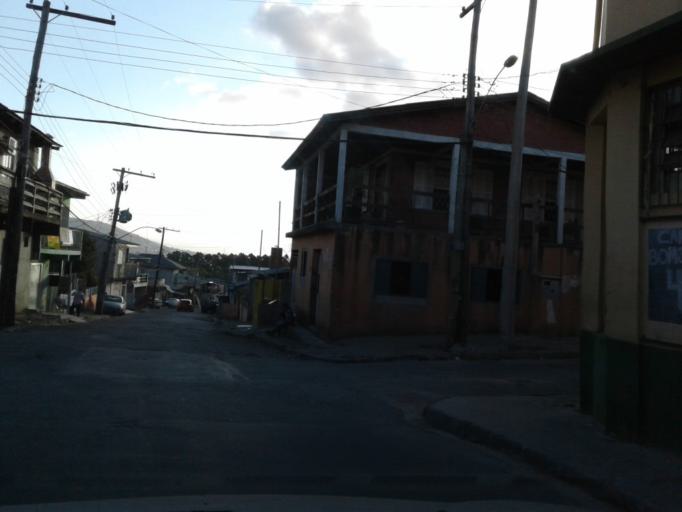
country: BR
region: Rio Grande do Sul
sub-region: Porto Alegre
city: Porto Alegre
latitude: -30.0490
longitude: -51.1506
